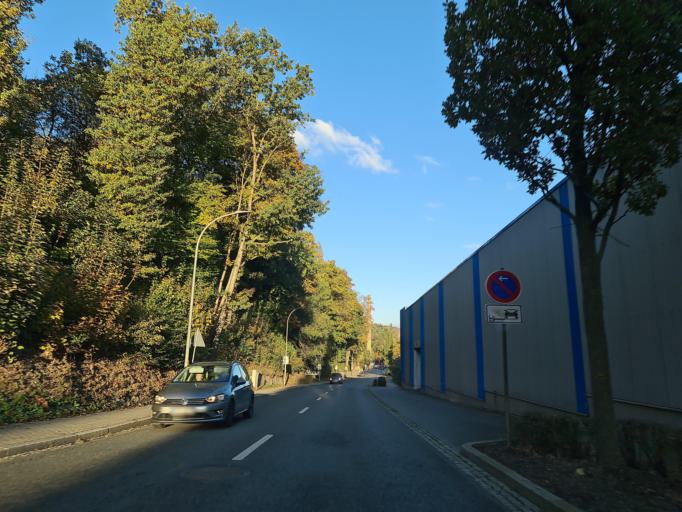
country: DE
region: Thuringia
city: Greiz
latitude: 50.6570
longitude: 12.1857
